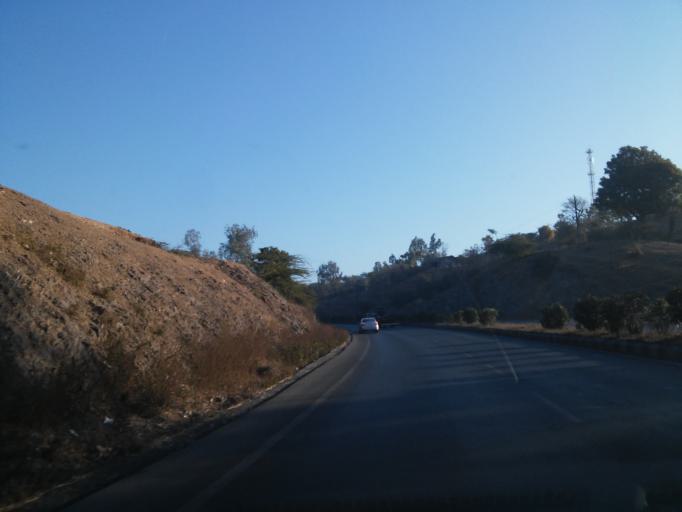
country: IN
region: Rajasthan
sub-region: Dungarpur
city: Dungarpur
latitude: 23.8902
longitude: 73.5397
